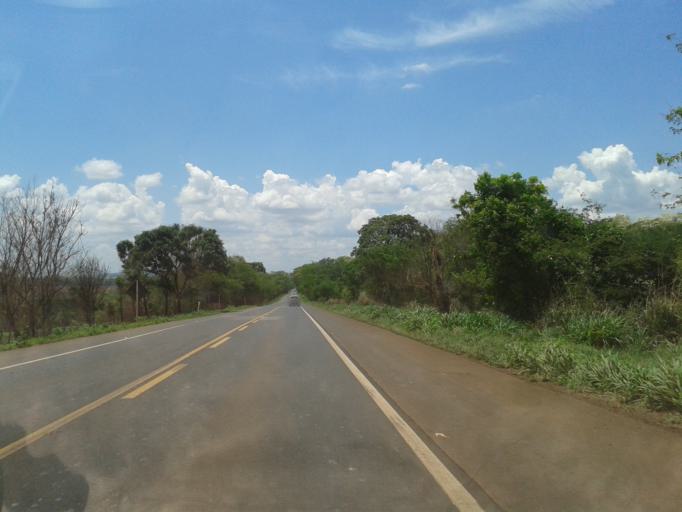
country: BR
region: Goias
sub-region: Goiatuba
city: Goiatuba
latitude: -18.2910
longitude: -49.6007
